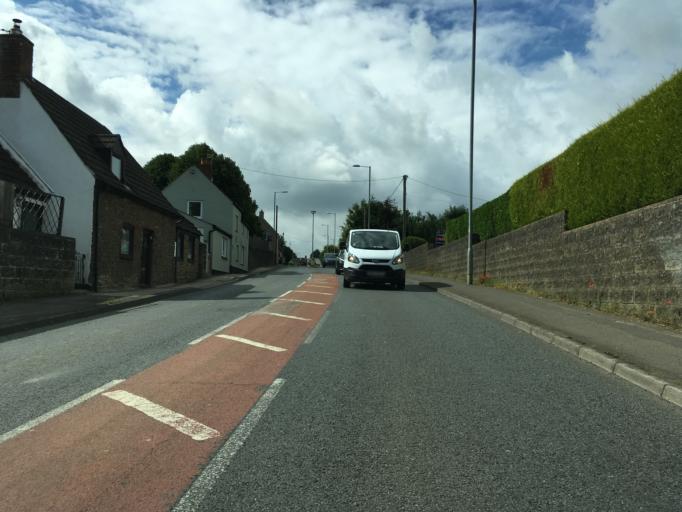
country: GB
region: England
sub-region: Borough of Swindon
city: Highworth
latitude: 51.6366
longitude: -1.7095
